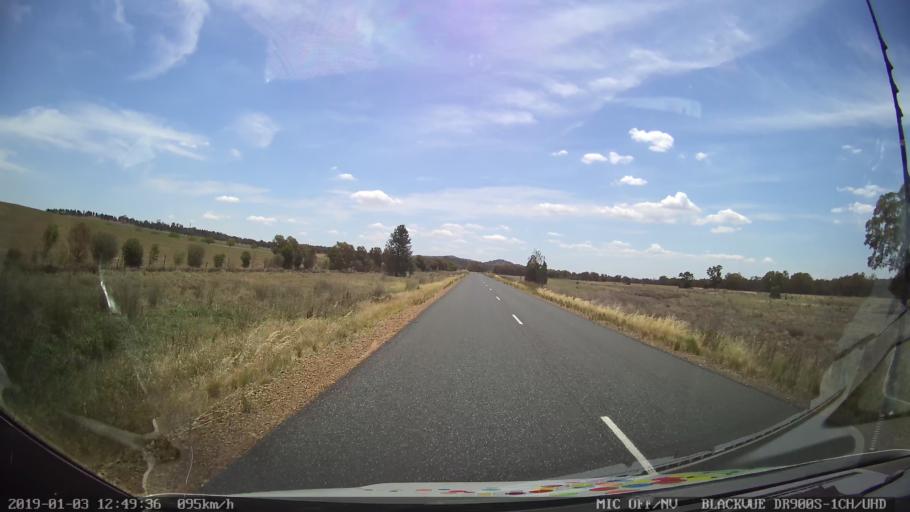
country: AU
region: New South Wales
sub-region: Weddin
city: Grenfell
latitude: -33.7015
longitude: 148.2625
